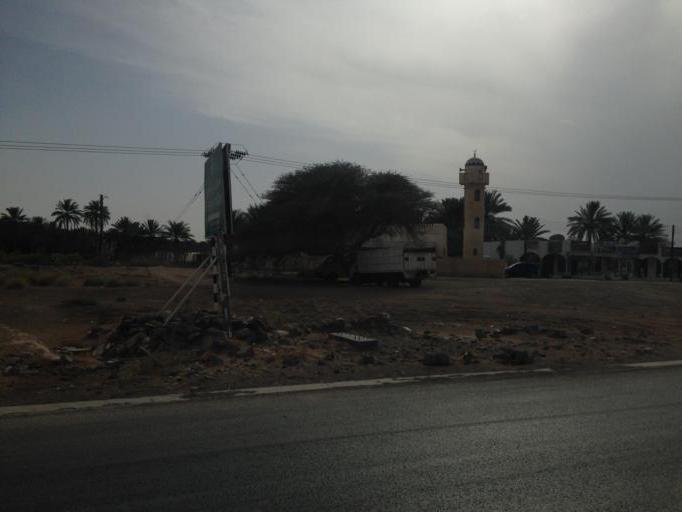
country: OM
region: Ash Sharqiyah
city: Badiyah
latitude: 22.5003
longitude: 58.7507
